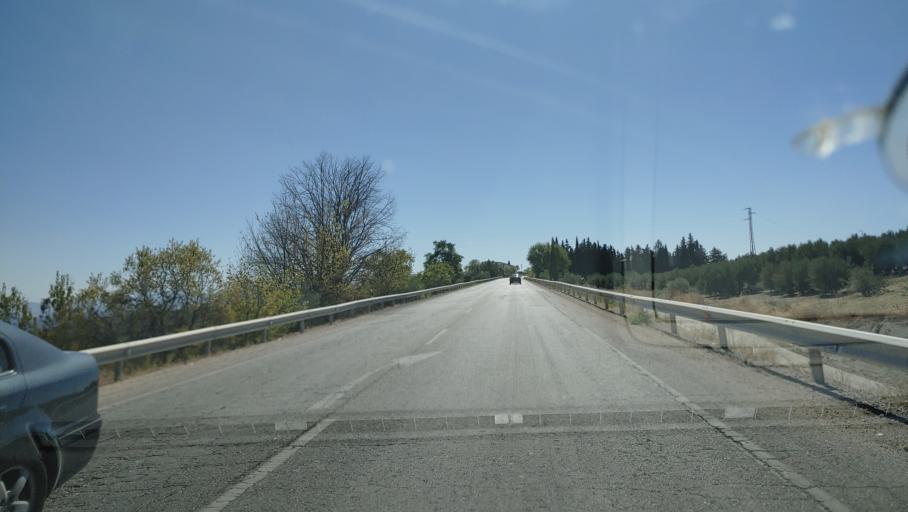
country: ES
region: Andalusia
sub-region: Provincia de Jaen
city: Villacarrillo
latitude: 38.1255
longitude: -3.0637
